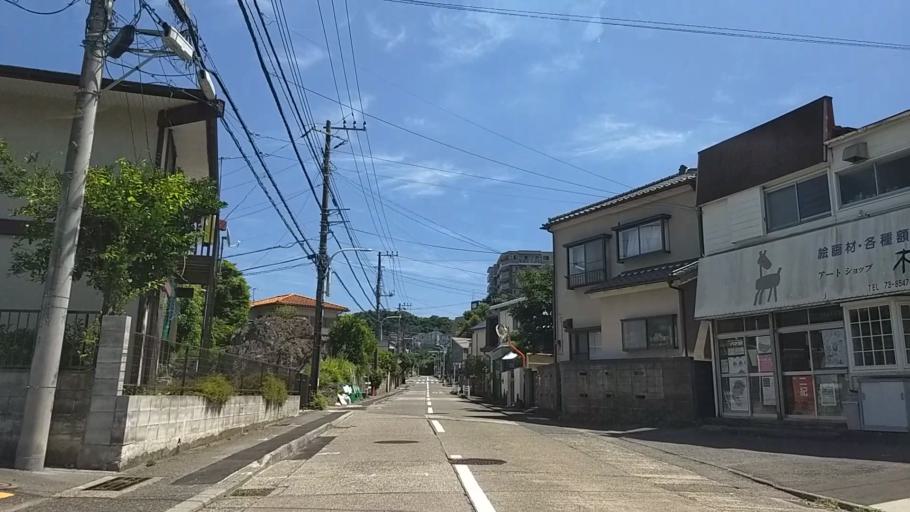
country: JP
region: Kanagawa
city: Zushi
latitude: 35.3071
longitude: 139.5955
